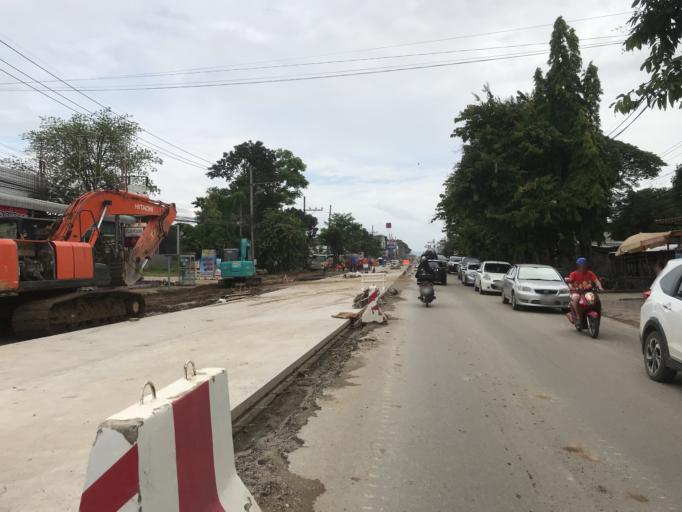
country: TH
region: Chiang Rai
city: Chiang Rai
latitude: 19.8971
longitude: 99.8319
